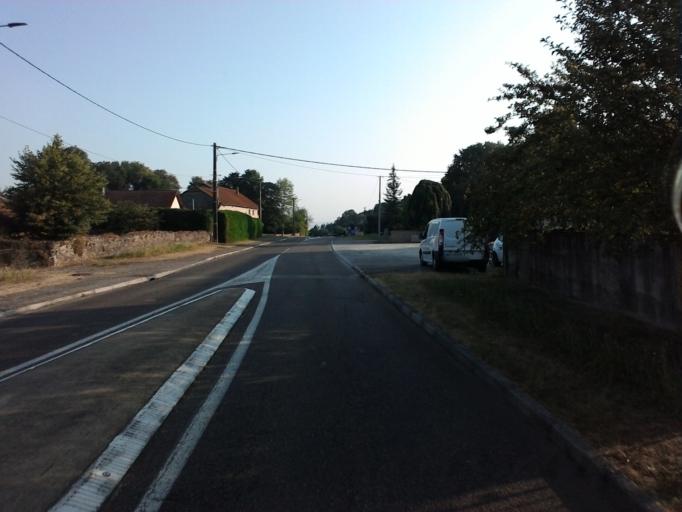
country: FR
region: Franche-Comte
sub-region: Departement de la Haute-Saone
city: Echenoz-la-Meline
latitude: 47.5892
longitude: 6.1386
